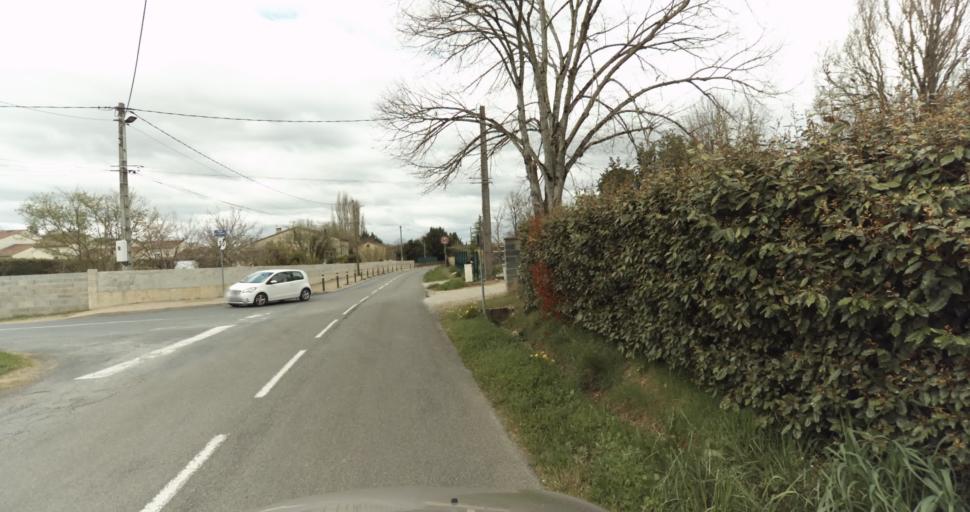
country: FR
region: Midi-Pyrenees
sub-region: Departement du Tarn
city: Puygouzon
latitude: 43.9119
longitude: 2.1686
